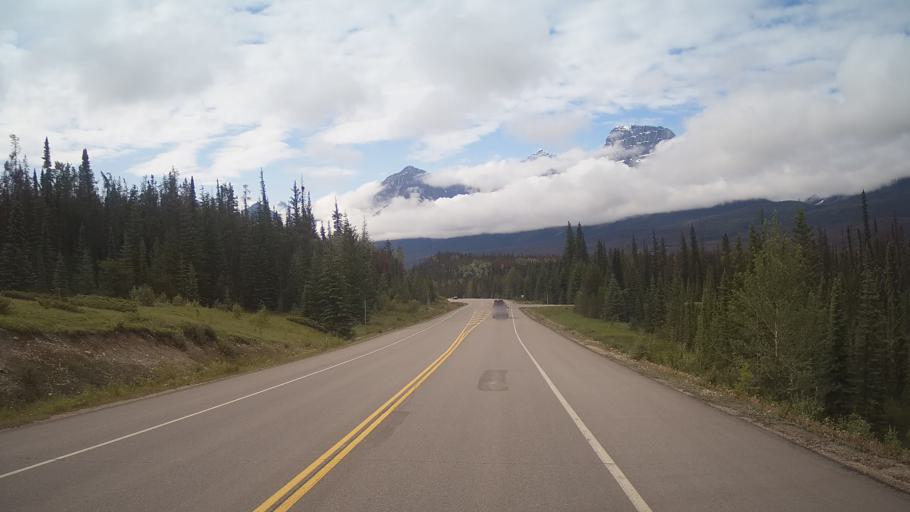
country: CA
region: Alberta
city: Jasper Park Lodge
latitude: 52.6707
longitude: -117.8817
